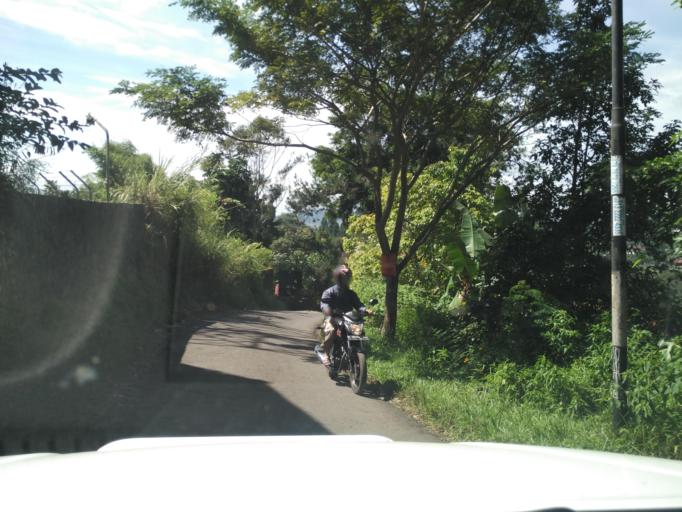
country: ID
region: West Java
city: Caringin
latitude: -6.7145
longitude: 107.0089
